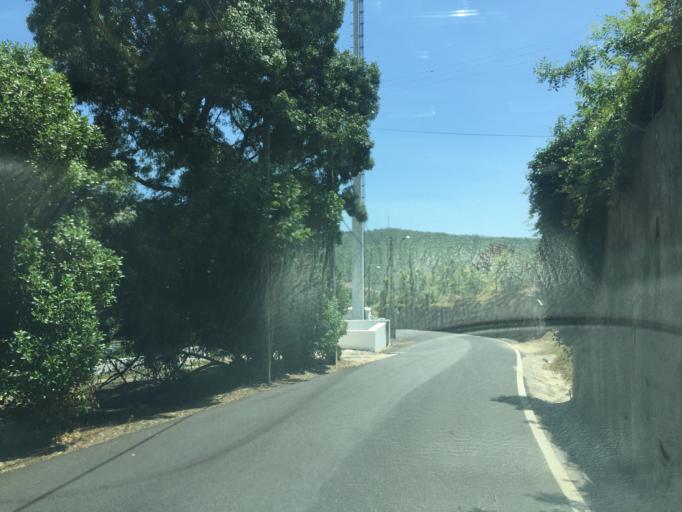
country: PT
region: Lisbon
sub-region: Mafra
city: Venda do Pinheiro
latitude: 38.8888
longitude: -9.2085
